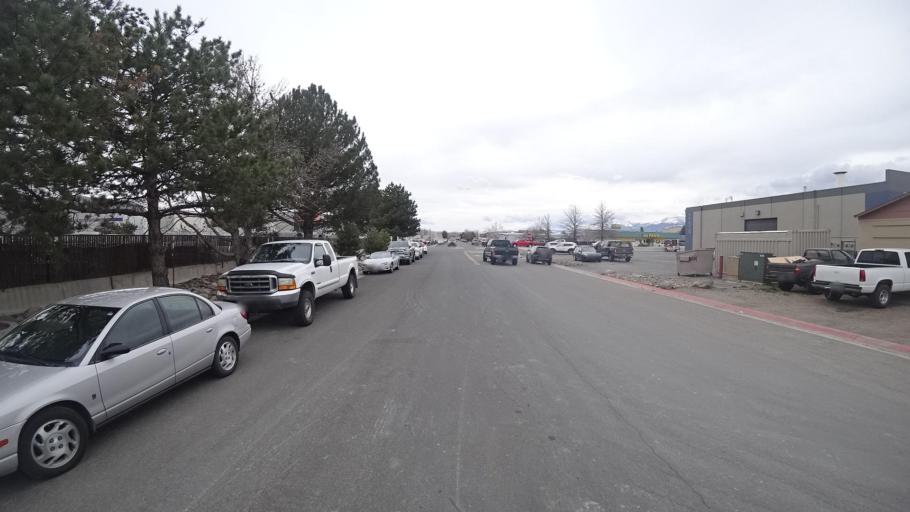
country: US
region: Nevada
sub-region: Washoe County
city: Sparks
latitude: 39.5281
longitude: -119.7384
